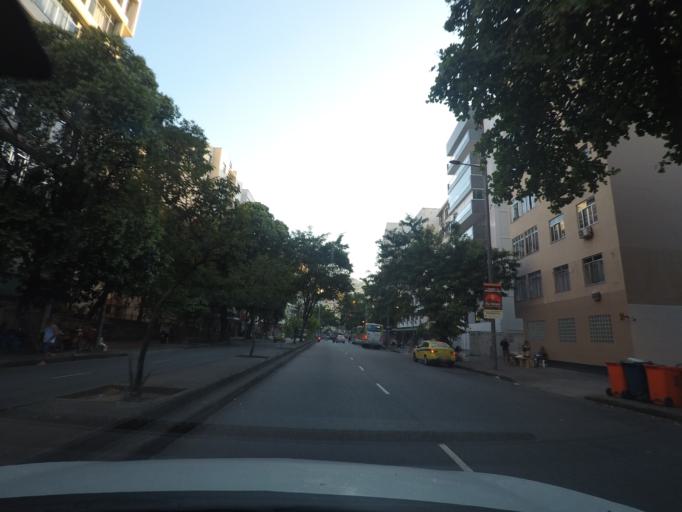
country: BR
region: Rio de Janeiro
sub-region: Rio De Janeiro
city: Rio de Janeiro
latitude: -22.9291
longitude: -43.2370
